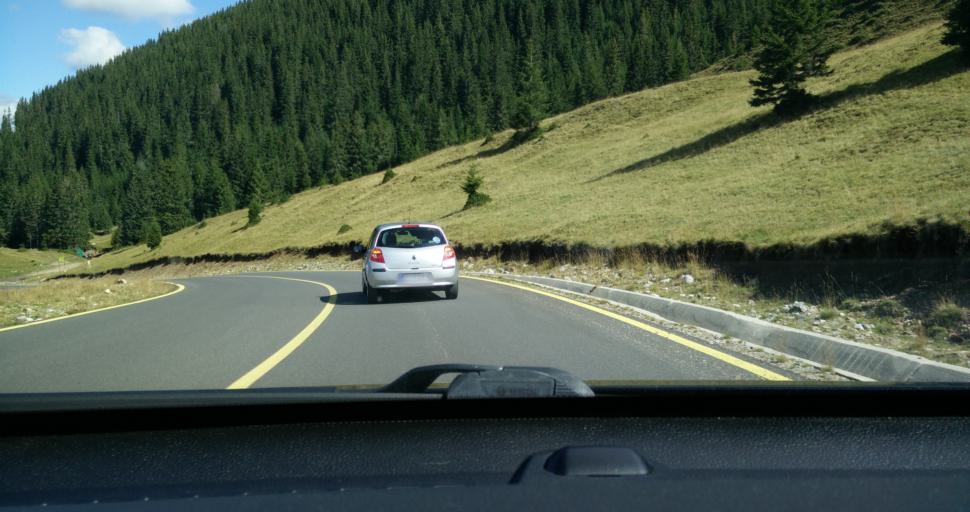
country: RO
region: Gorj
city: Novaci-Straini
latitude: 45.3899
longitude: 23.6439
